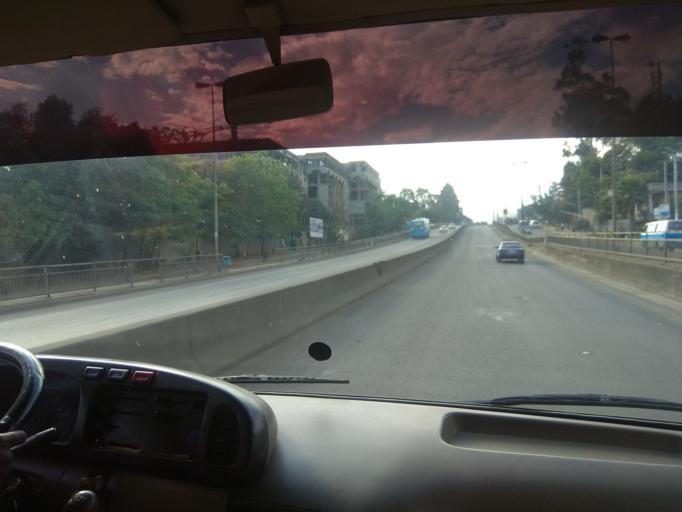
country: ET
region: Adis Abeba
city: Addis Ababa
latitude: 9.0177
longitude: 38.7175
